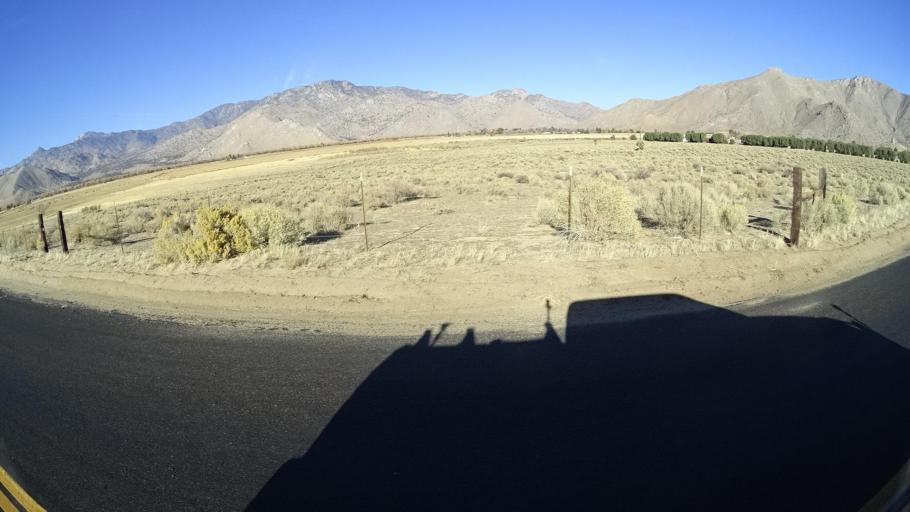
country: US
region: California
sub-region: Kern County
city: Weldon
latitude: 35.6526
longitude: -118.2809
